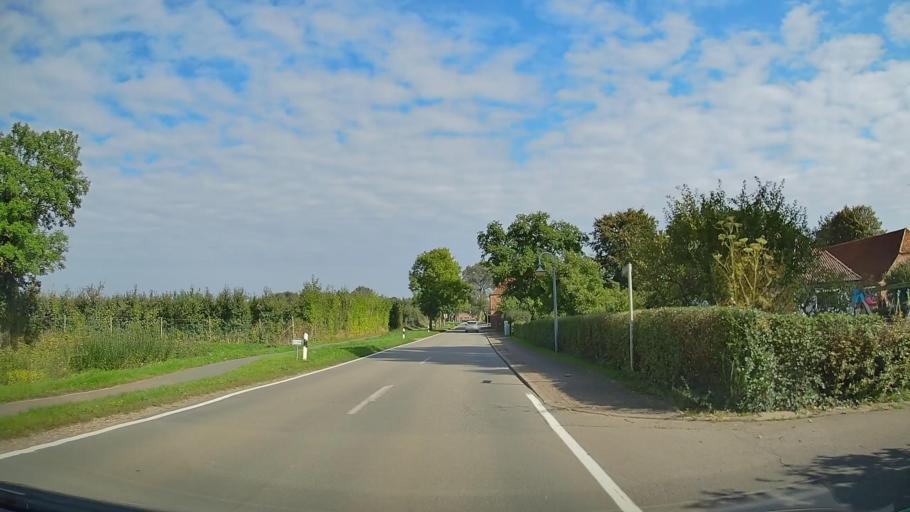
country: DE
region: Schleswig-Holstein
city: Oldenburg in Holstein
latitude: 54.3230
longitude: 10.8883
